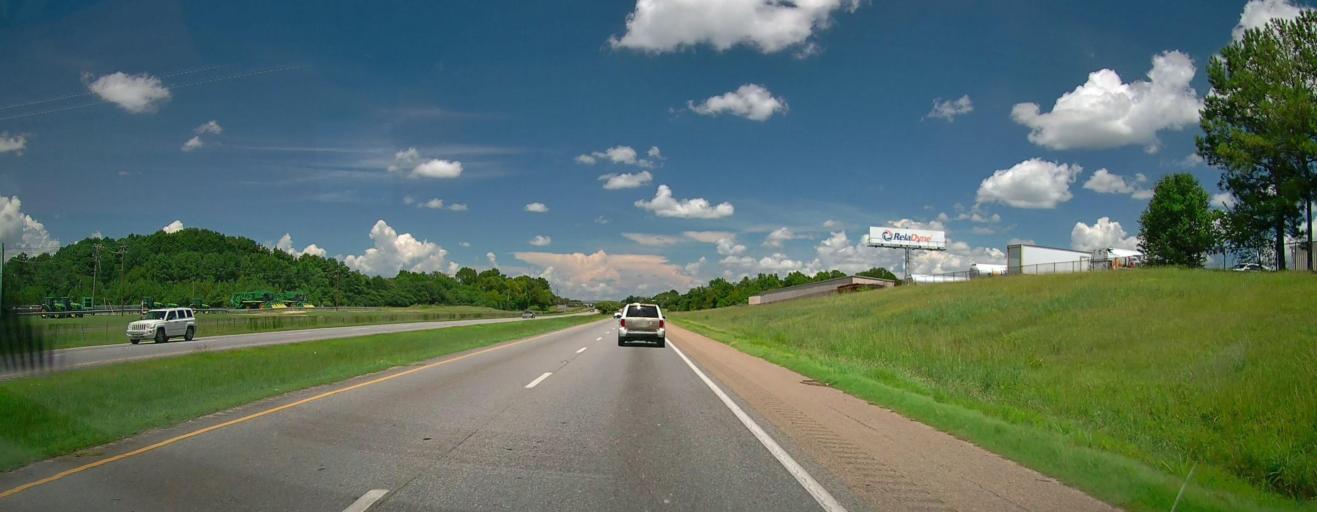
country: US
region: Alabama
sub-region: Montgomery County
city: Montgomery
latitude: 32.4132
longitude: -86.3000
